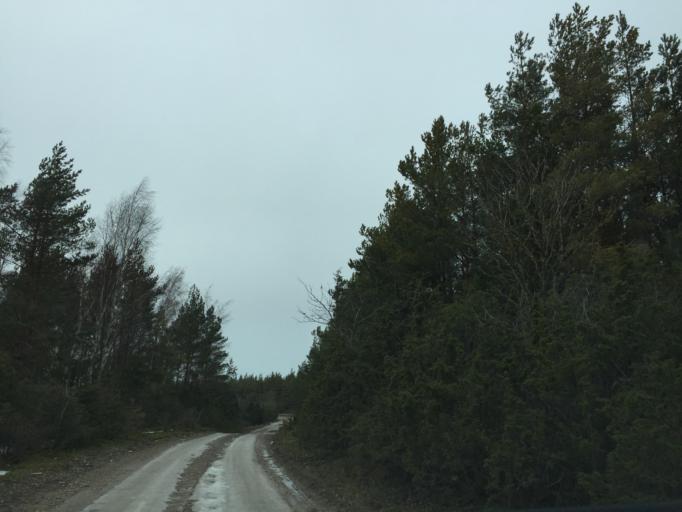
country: EE
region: Saare
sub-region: Kuressaare linn
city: Kuressaare
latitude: 58.5004
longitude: 21.9201
